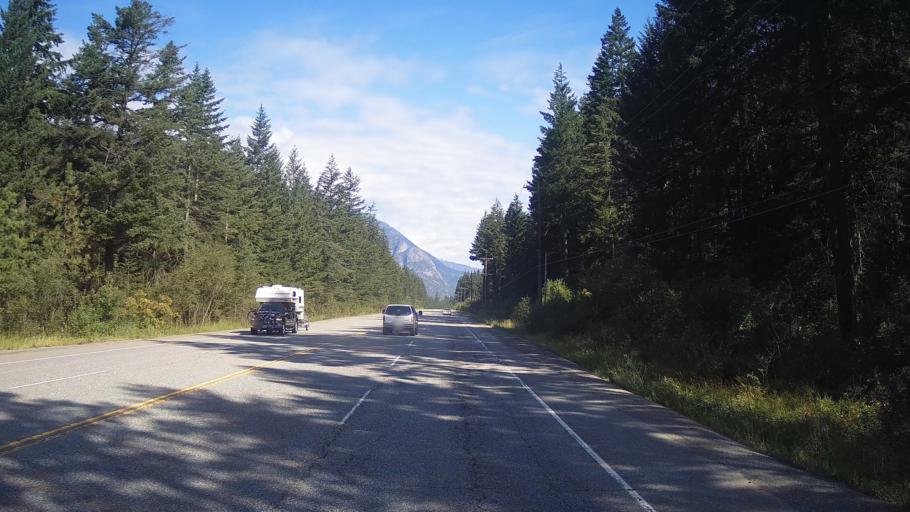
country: CA
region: British Columbia
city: Hope
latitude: 50.0404
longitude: -121.5356
